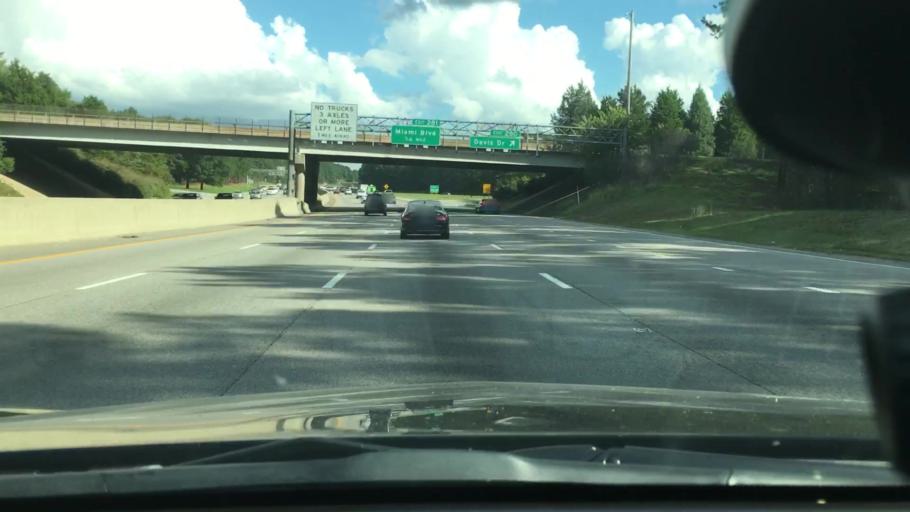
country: US
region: North Carolina
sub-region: Wake County
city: Morrisville
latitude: 35.8947
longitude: -78.8610
